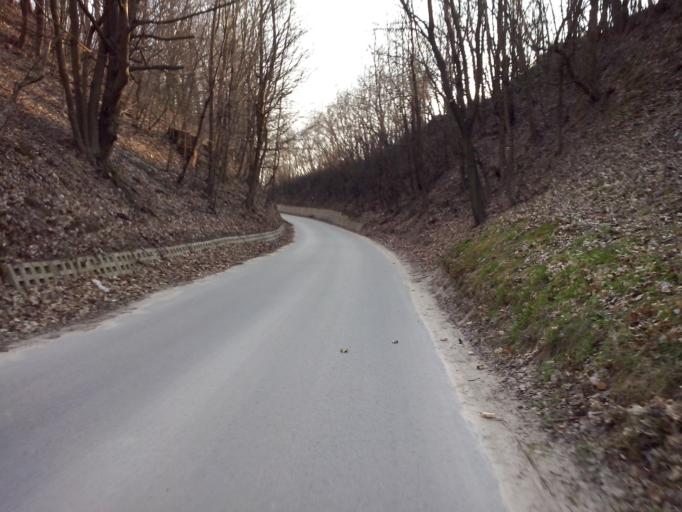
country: PL
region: Subcarpathian Voivodeship
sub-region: Powiat nizanski
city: Krzeszow
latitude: 50.4088
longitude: 22.3521
